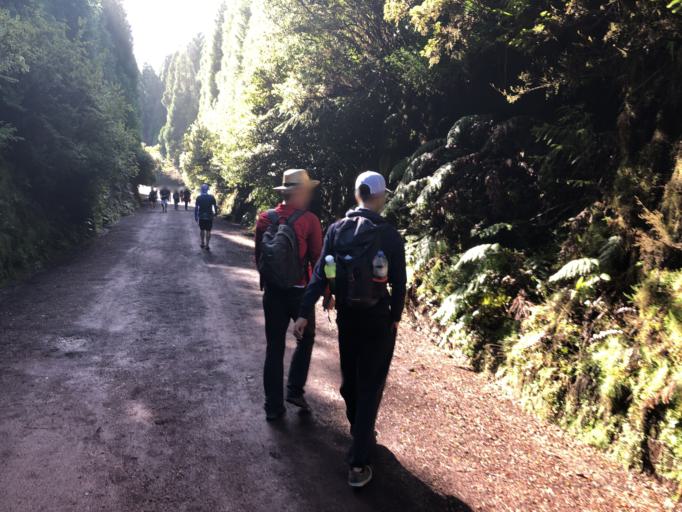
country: PT
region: Azores
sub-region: Ponta Delgada
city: Arrifes
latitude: 37.8408
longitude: -25.7605
